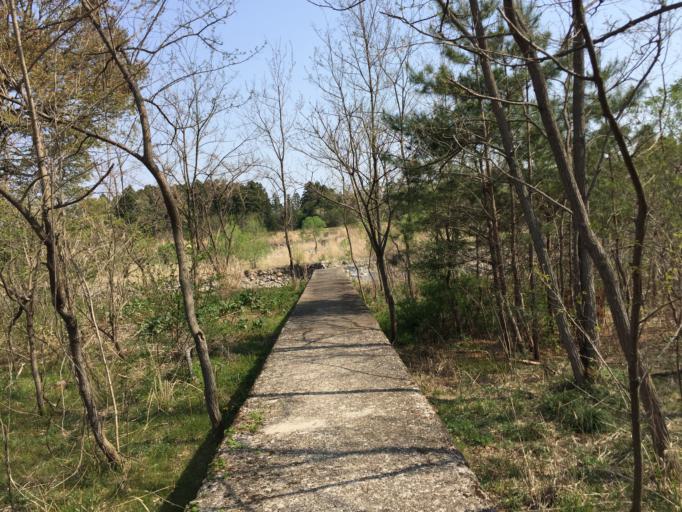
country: JP
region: Fukushima
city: Fukushima-shi
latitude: 37.7324
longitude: 140.3774
